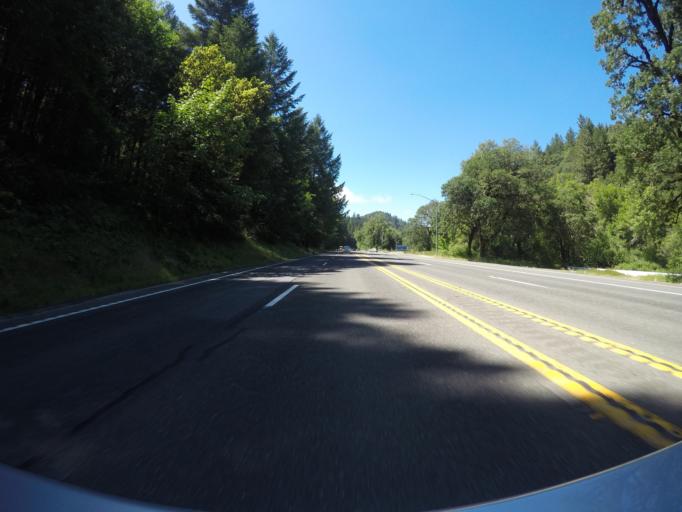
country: US
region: California
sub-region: Mendocino County
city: Laytonville
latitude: 39.5865
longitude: -123.4483
